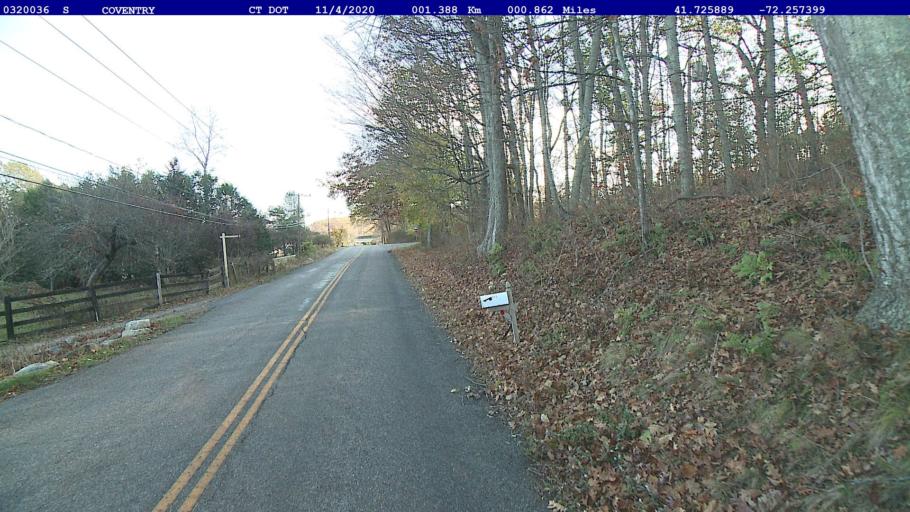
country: US
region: Connecticut
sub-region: Tolland County
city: Mansfield City
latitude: 41.7259
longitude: -72.2574
